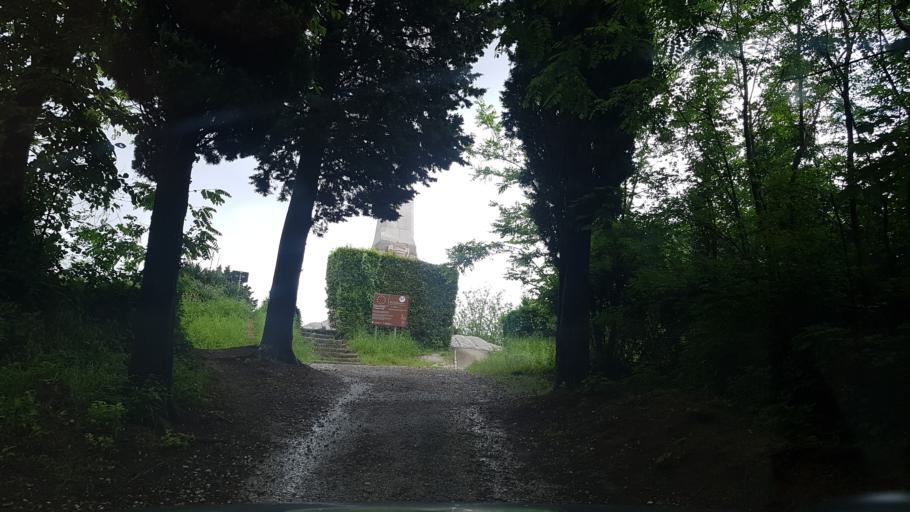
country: IT
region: Friuli Venezia Giulia
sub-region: Provincia di Gorizia
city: Gorizia
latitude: 45.9447
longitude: 13.5910
